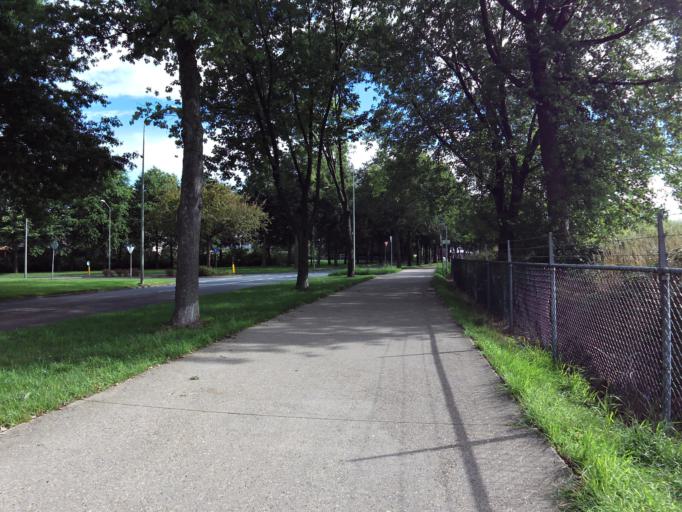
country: NL
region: Limburg
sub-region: Gemeente Brunssum
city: Brunssum
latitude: 50.9185
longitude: 5.9642
